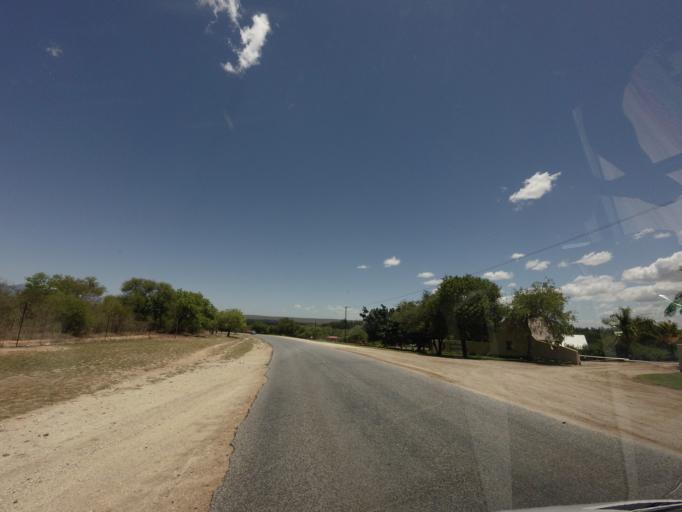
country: ZA
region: Limpopo
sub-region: Mopani District Municipality
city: Hoedspruit
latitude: -24.3723
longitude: 30.7304
